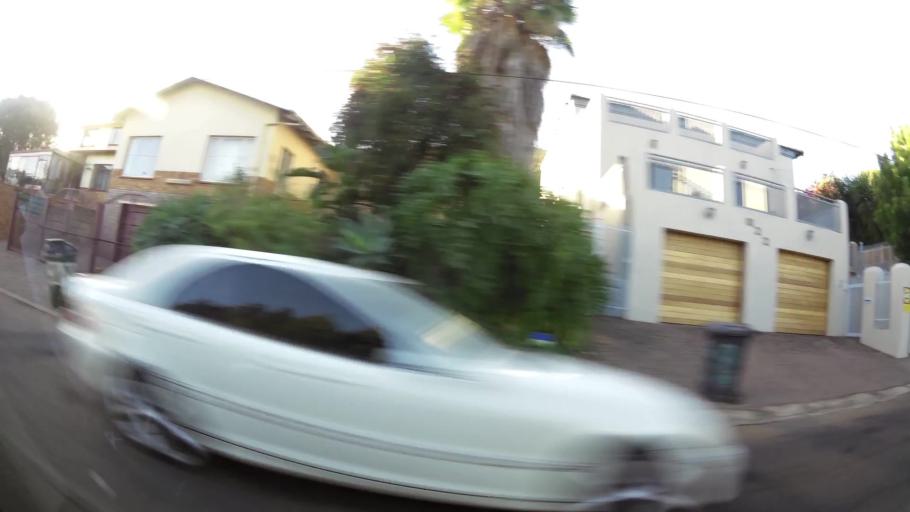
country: ZA
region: Gauteng
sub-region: City of Tshwane Metropolitan Municipality
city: Pretoria
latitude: -25.6960
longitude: 28.2195
